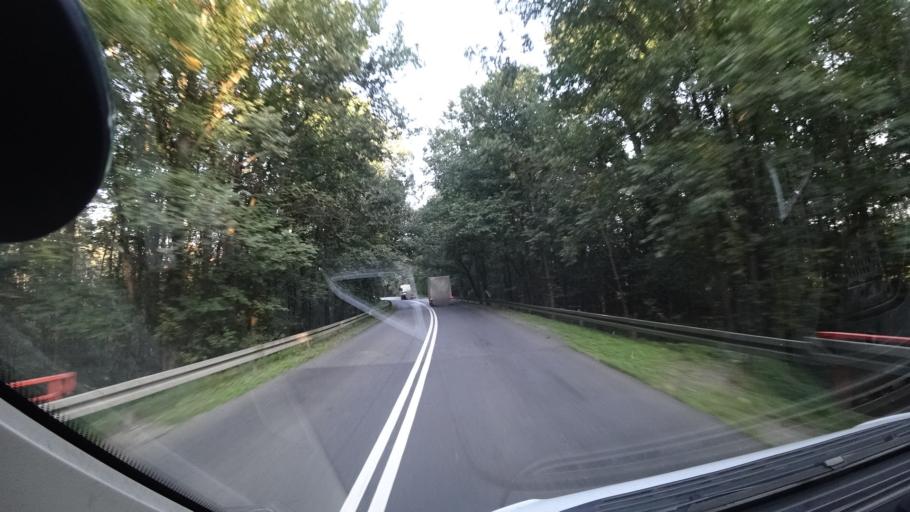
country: PL
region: Opole Voivodeship
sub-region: Powiat kedzierzynsko-kozielski
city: Dziergowice
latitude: 50.2819
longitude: 18.2962
